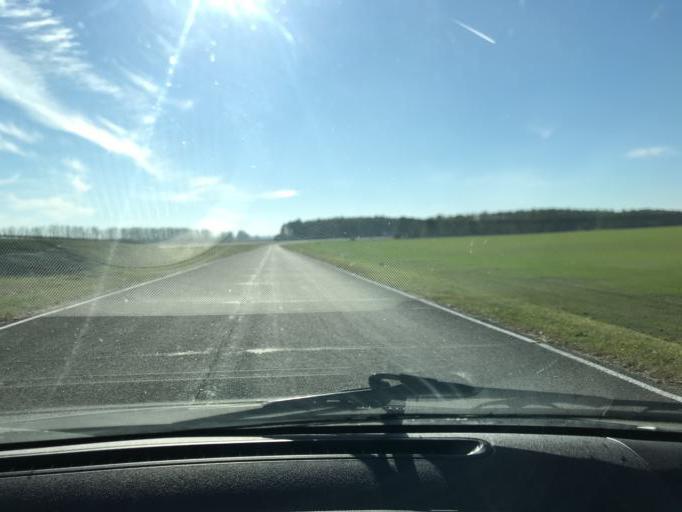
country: BY
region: Brest
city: Ivatsevichy
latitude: 52.7008
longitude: 25.3602
